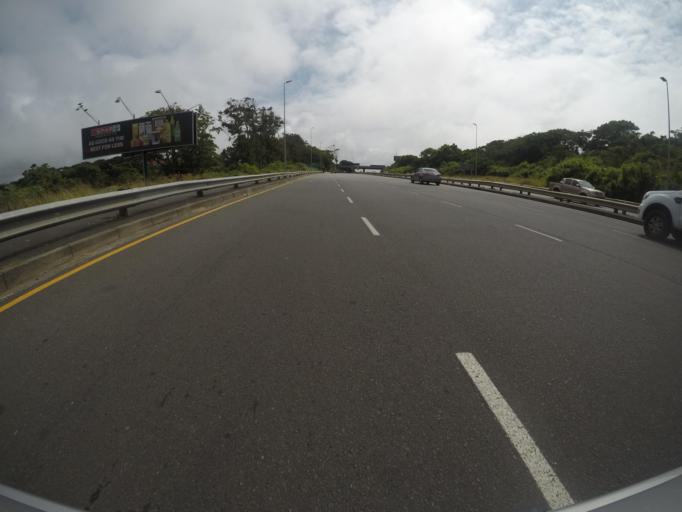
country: ZA
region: Eastern Cape
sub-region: Buffalo City Metropolitan Municipality
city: East London
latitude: -33.0004
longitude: 27.9136
